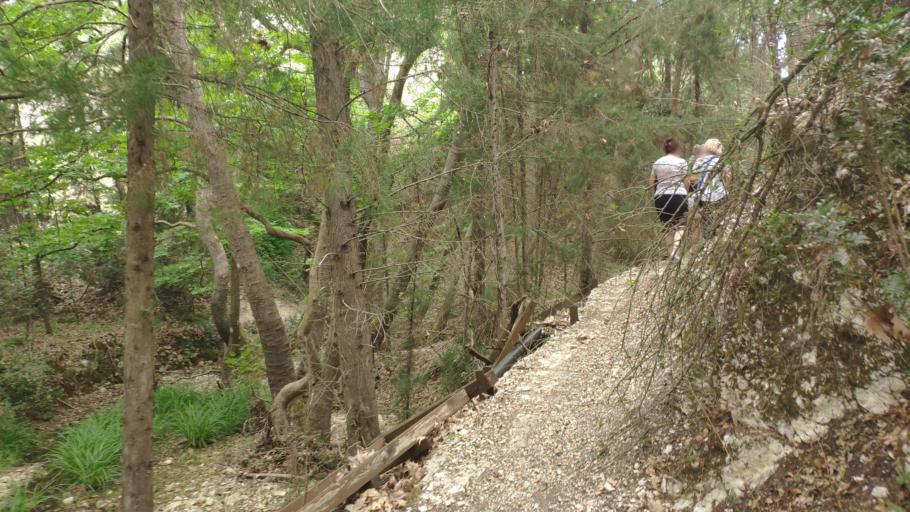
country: GR
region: Ionian Islands
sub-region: Lefkada
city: Lefkada
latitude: 38.8007
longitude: 20.6703
